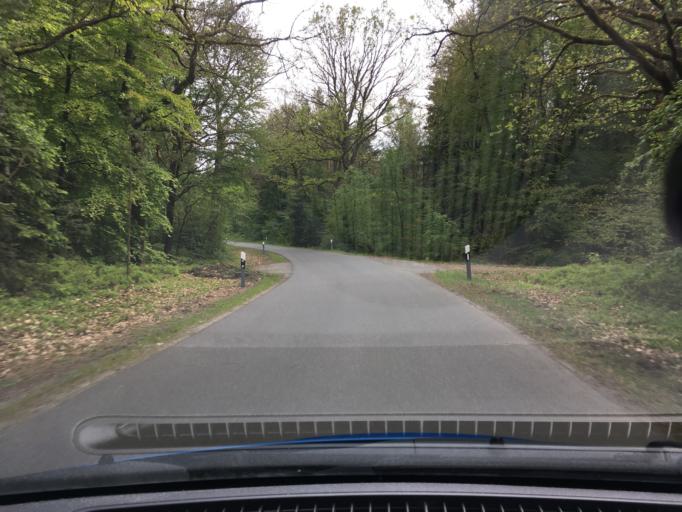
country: DE
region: Lower Saxony
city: Eimke
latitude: 52.9784
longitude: 10.2495
